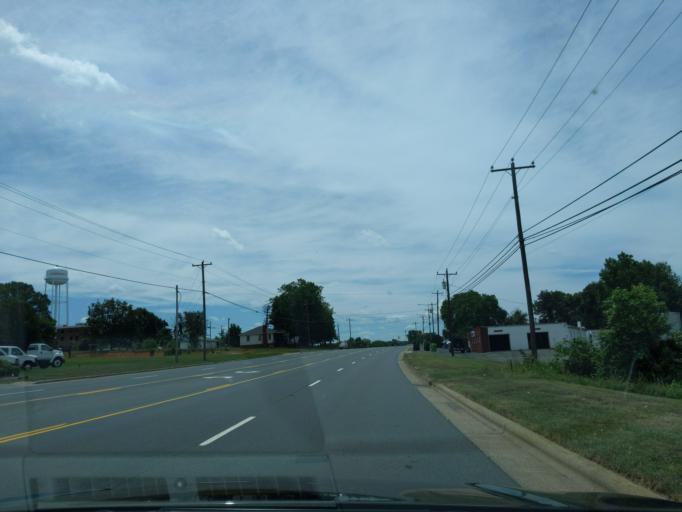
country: US
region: North Carolina
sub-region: Stanly County
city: Albemarle
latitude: 35.4015
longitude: -80.2010
